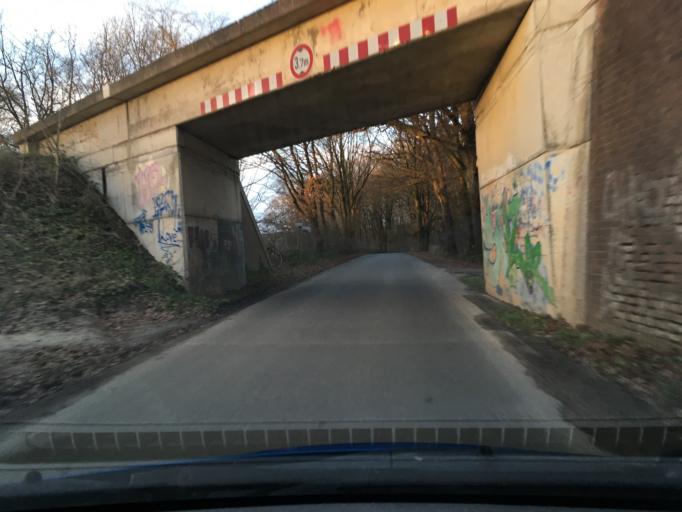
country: DE
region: Lower Saxony
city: Amelinghausen
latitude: 53.1360
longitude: 10.2048
